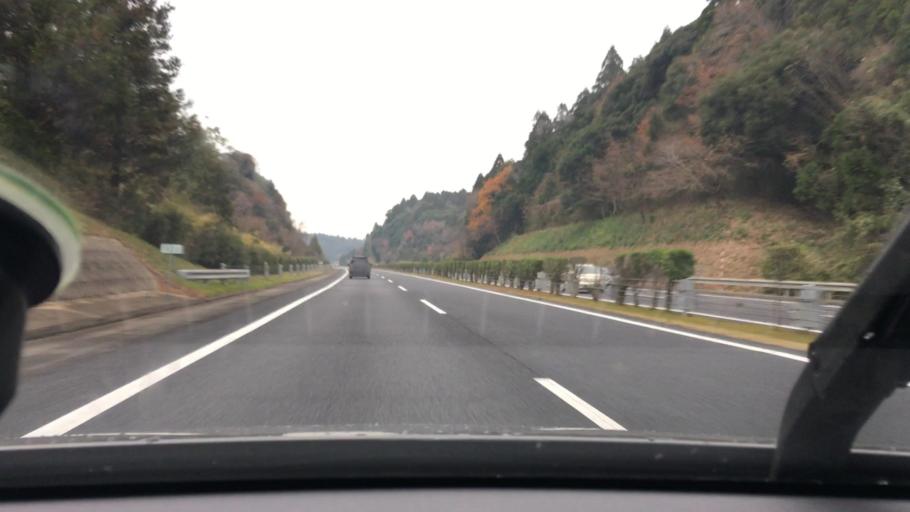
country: JP
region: Chiba
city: Sawara
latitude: 35.8578
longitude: 140.5226
